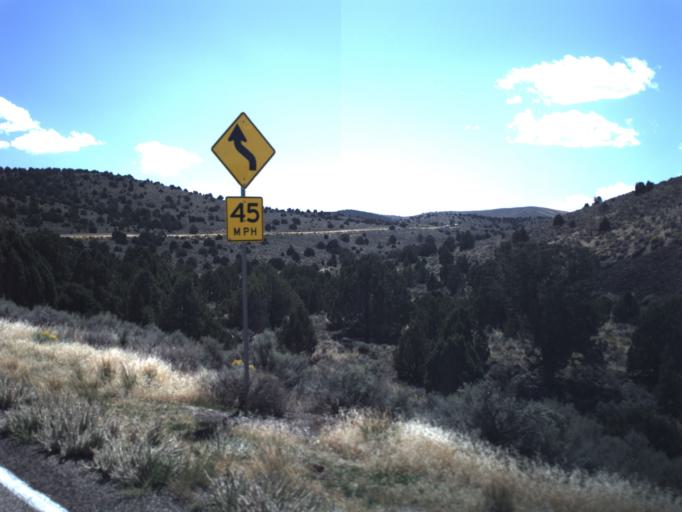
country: US
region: Utah
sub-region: Beaver County
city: Milford
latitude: 38.1241
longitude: -112.9536
